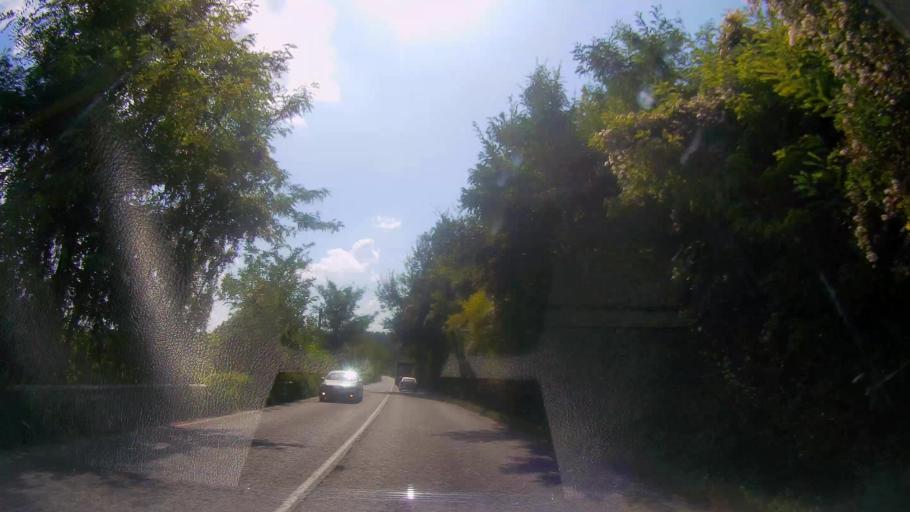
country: BG
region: Veliko Turnovo
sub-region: Obshtina Polski Trumbesh
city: Polski Trumbesh
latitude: 43.4365
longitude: 25.6545
